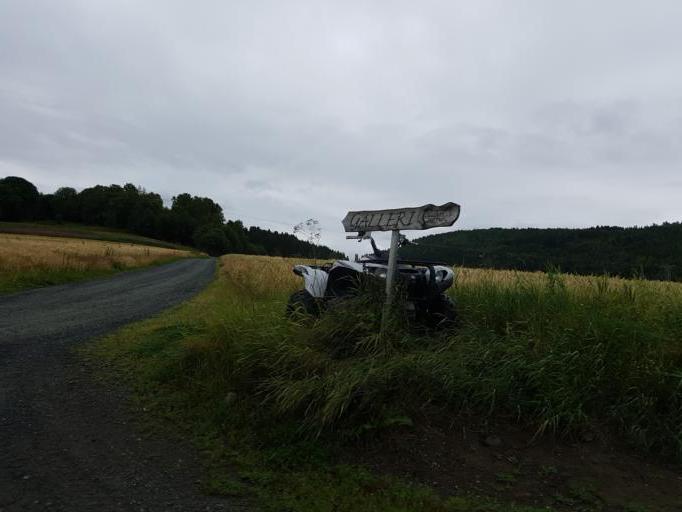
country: NO
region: Nord-Trondelag
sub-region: Levanger
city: Levanger
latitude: 63.7201
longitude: 11.2565
